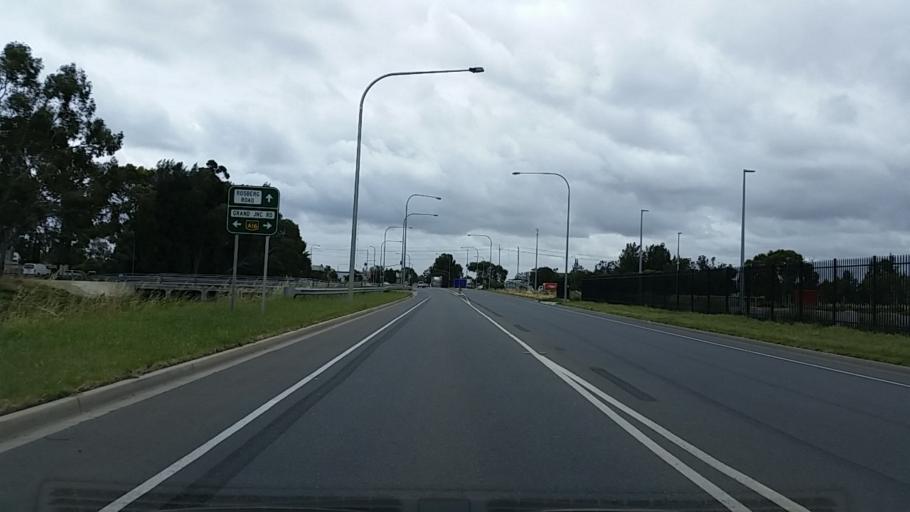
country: AU
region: South Australia
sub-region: Port Adelaide Enfield
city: Blair Athol
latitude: -34.8520
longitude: 138.5741
